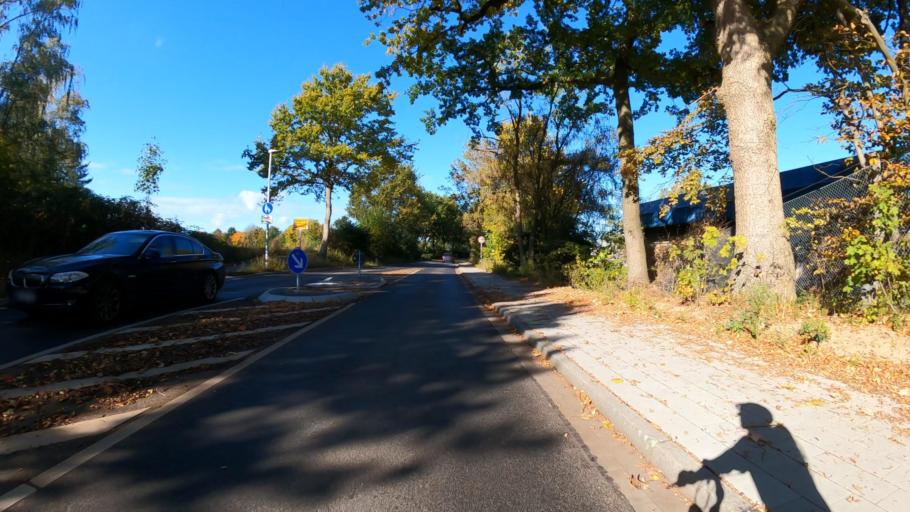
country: DE
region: Schleswig-Holstein
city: Ahrensburg
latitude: 53.6854
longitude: 10.2286
